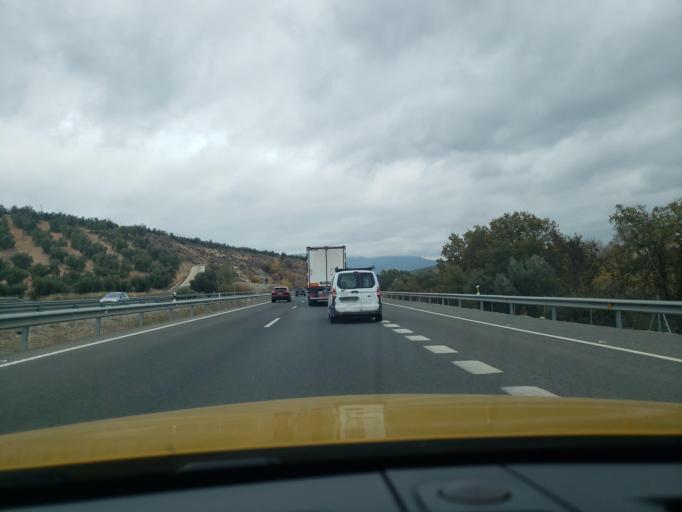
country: ES
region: Andalusia
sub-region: Provincia de Granada
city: Deifontes
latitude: 37.3289
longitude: -3.6330
